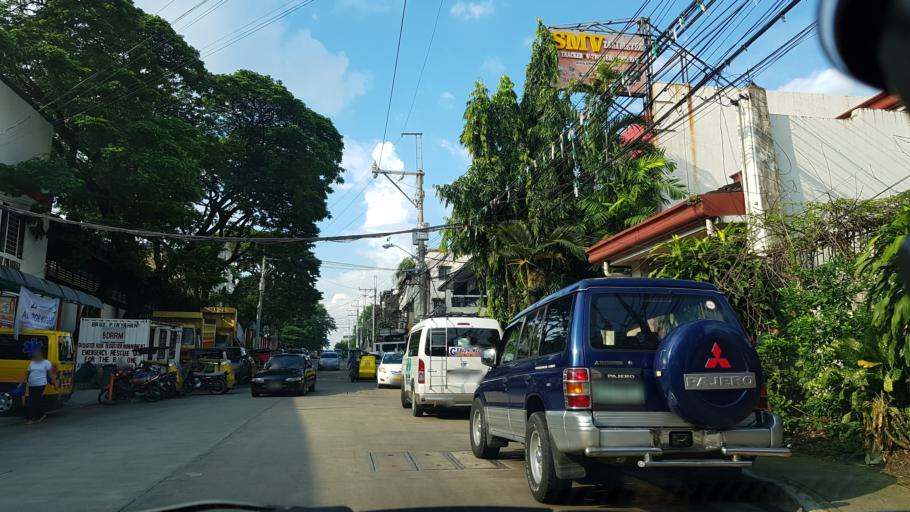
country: PH
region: Metro Manila
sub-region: Quezon City
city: Quezon City
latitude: 14.6342
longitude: 121.0473
